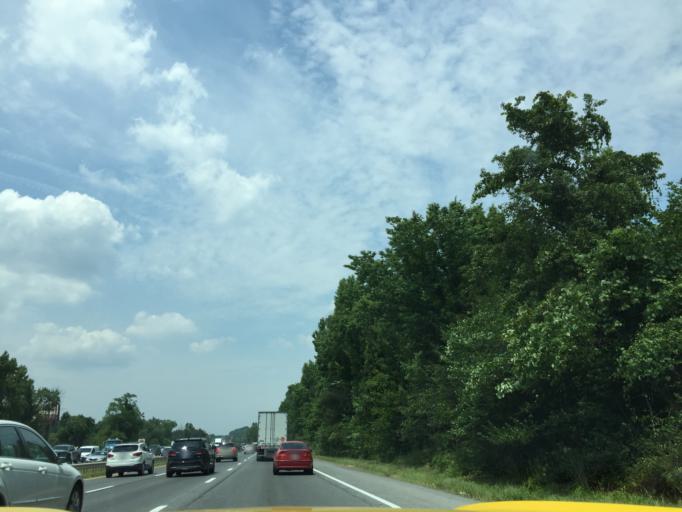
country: US
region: Maryland
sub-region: Prince George's County
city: Friendly
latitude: 38.7626
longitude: -76.9938
